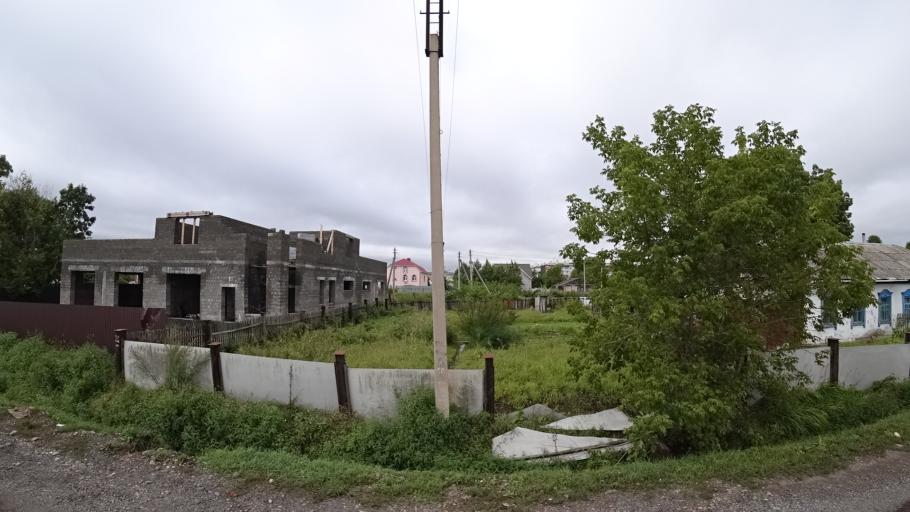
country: RU
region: Primorskiy
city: Monastyrishche
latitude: 44.2009
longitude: 132.4493
